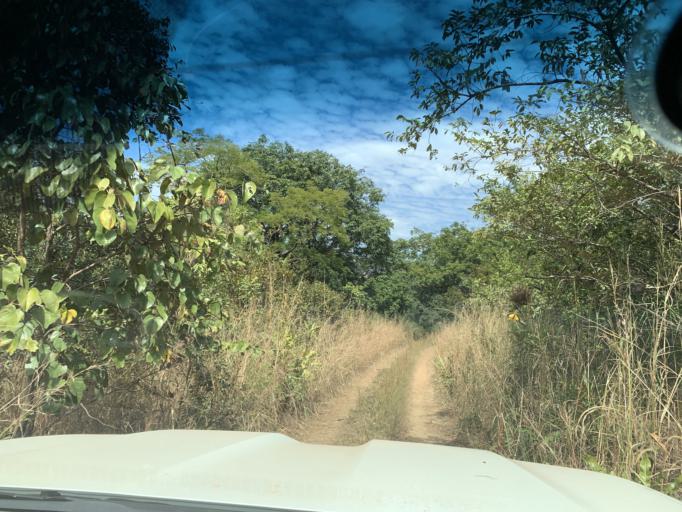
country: GN
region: Mamou
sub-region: Pita
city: Pita
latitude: 10.9932
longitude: -12.4889
